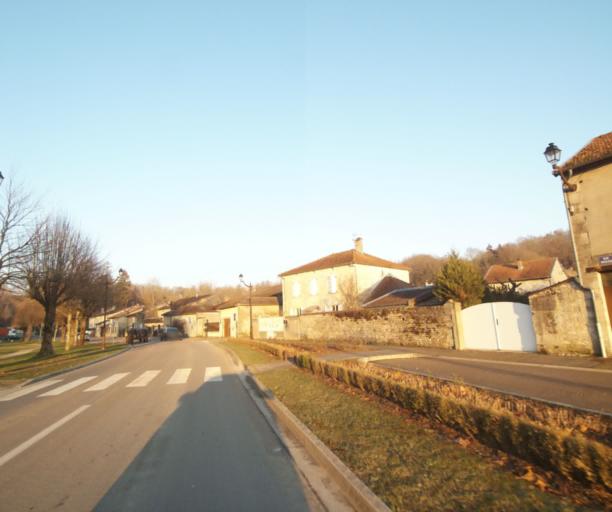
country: FR
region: Champagne-Ardenne
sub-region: Departement de la Haute-Marne
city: Bienville
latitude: 48.6081
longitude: 5.0452
